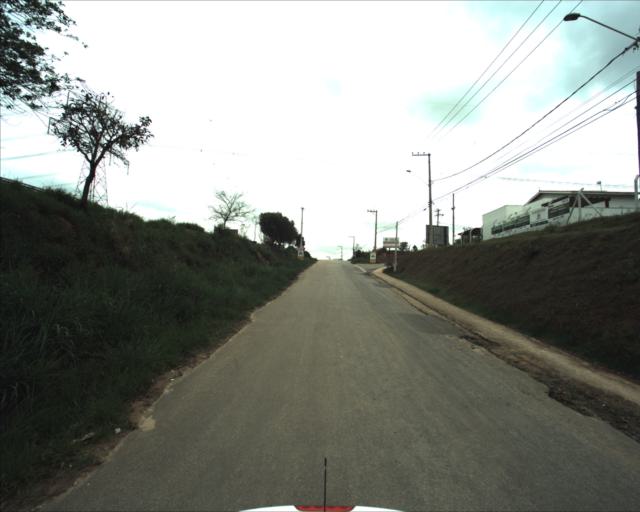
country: BR
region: Sao Paulo
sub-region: Sorocaba
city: Sorocaba
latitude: -23.4550
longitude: -47.3829
